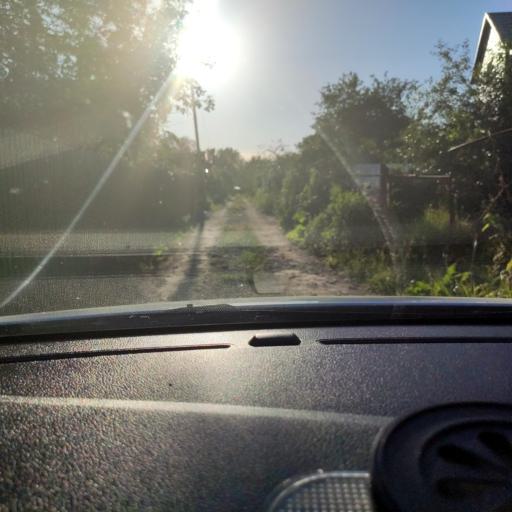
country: RU
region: Tatarstan
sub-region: Gorod Kazan'
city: Kazan
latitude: 55.8534
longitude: 49.1705
